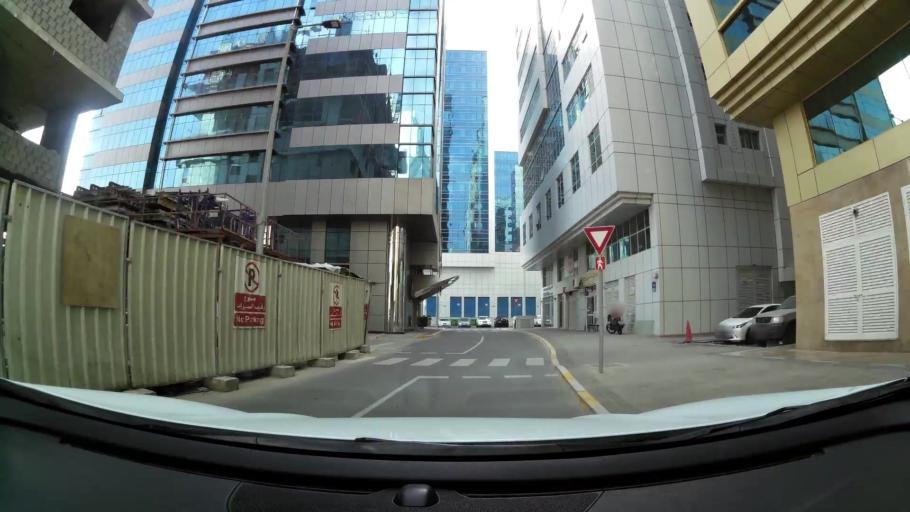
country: AE
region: Abu Dhabi
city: Abu Dhabi
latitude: 24.4665
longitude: 54.3860
